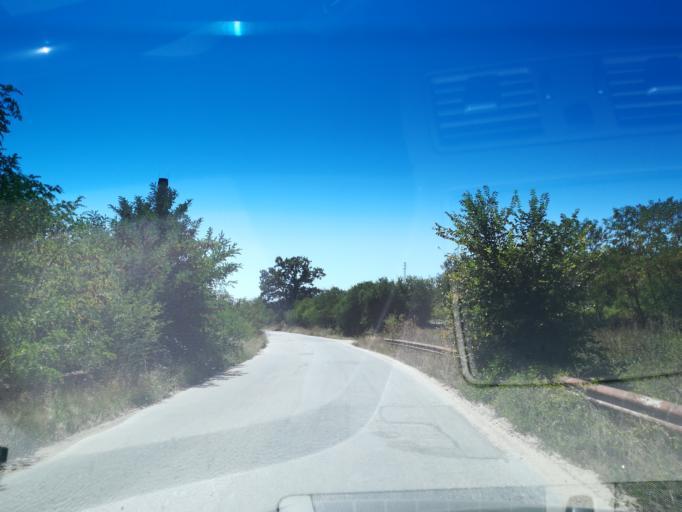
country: BG
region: Pazardzhik
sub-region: Obshtina Strelcha
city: Strelcha
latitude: 42.5225
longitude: 24.3218
